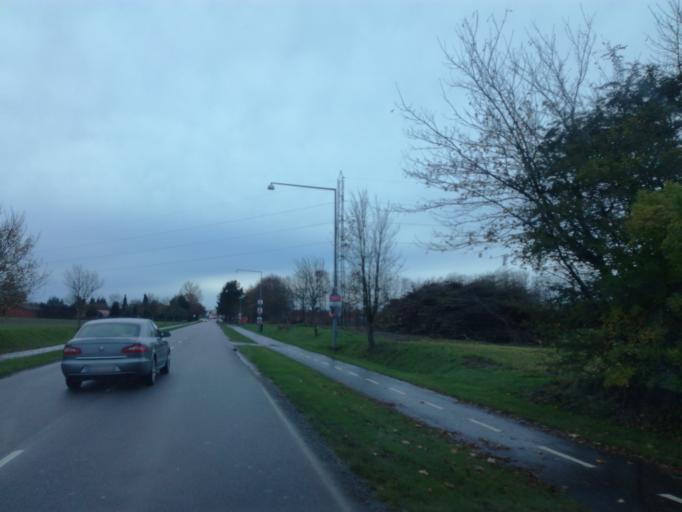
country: DK
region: South Denmark
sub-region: Vejle Kommune
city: Brejning
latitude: 55.6556
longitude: 9.6681
